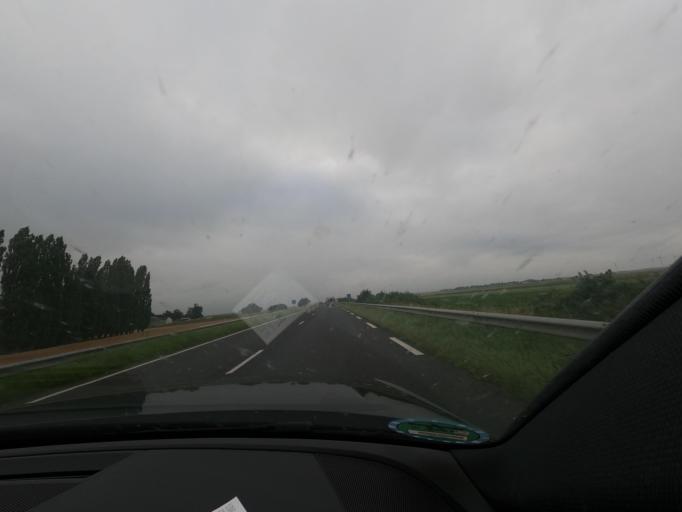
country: FR
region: Picardie
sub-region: Departement de la Somme
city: Rosieres-en-Santerre
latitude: 49.7486
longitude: 2.6644
